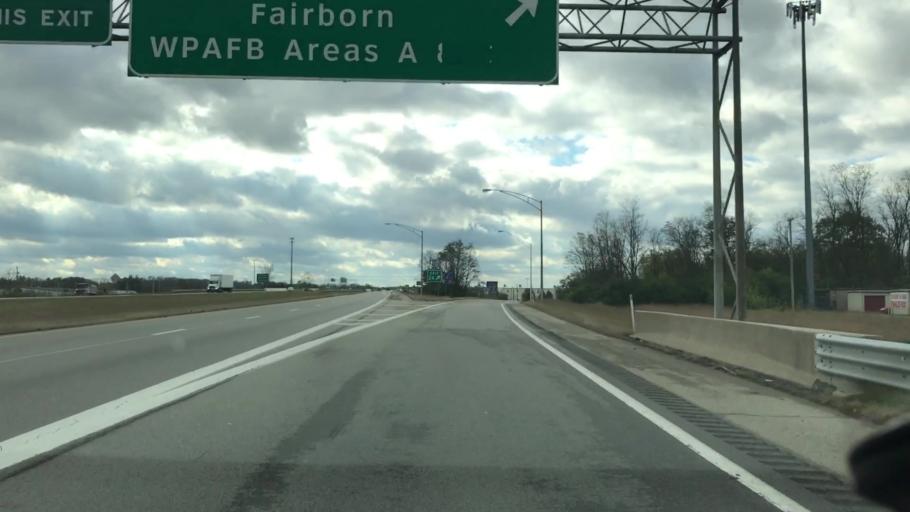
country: US
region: Ohio
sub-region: Clark County
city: Holiday Valley
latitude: 39.8481
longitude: -83.9943
